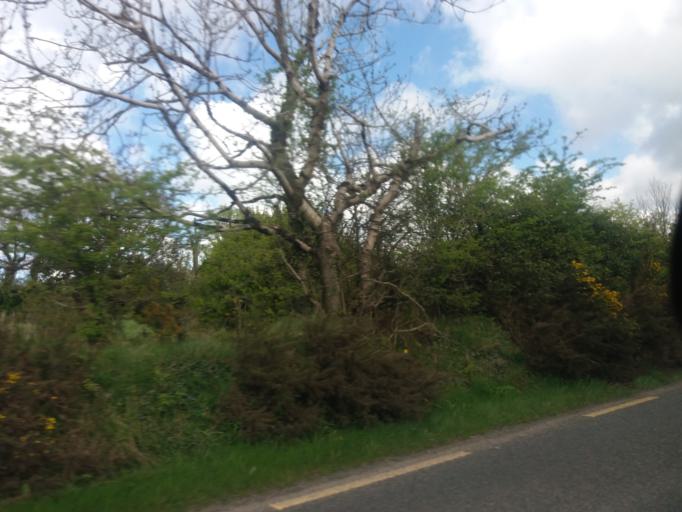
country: IE
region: Leinster
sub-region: Loch Garman
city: Loch Garman
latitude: 52.3019
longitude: -6.5608
